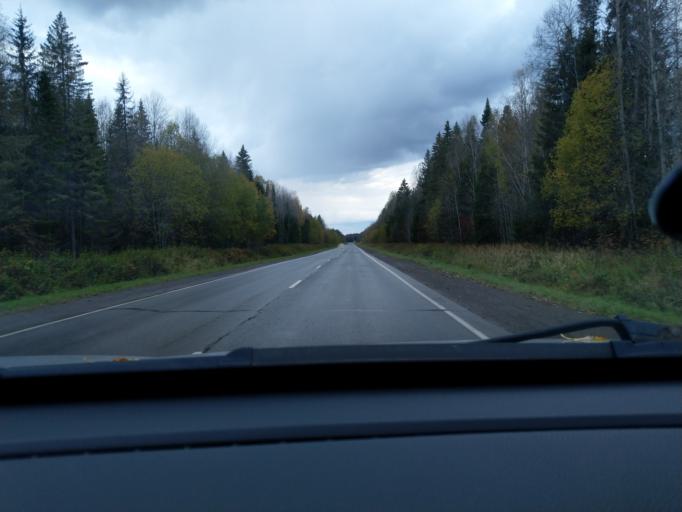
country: RU
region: Perm
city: Dobryanka
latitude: 58.4497
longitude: 56.5142
